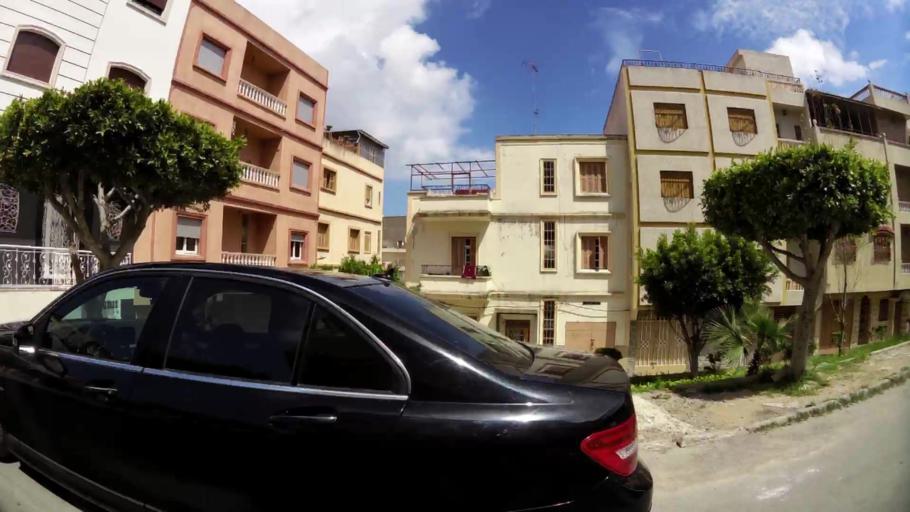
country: MA
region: Tanger-Tetouan
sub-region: Tanger-Assilah
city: Tangier
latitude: 35.7604
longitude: -5.8172
